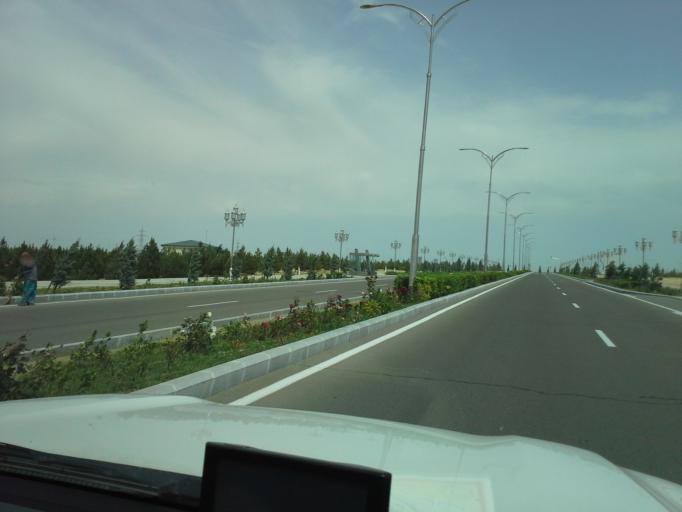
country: TM
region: Balkan
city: Turkmenbasy
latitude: 39.9658
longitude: 52.8600
